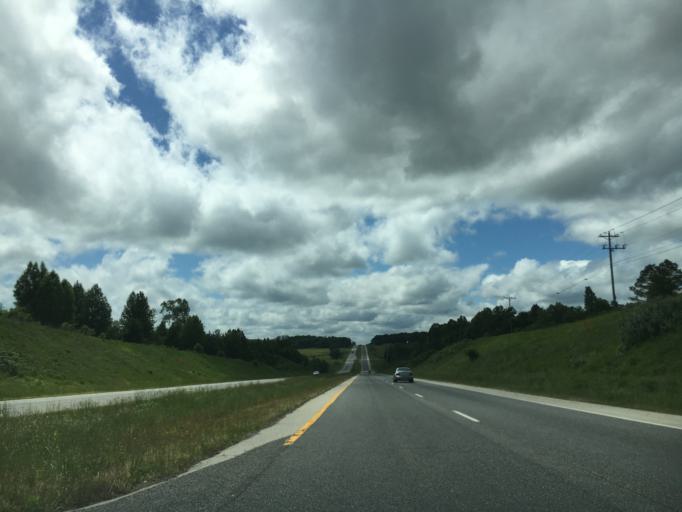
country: US
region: Virginia
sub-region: Mecklenburg County
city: Boydton
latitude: 36.6715
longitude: -78.2668
